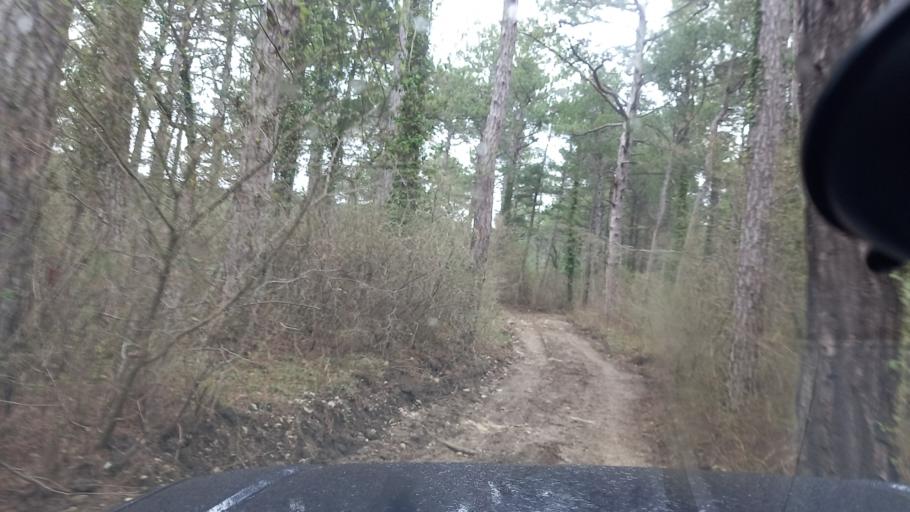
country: RU
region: Krasnodarskiy
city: Arkhipo-Osipovka
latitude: 44.3694
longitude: 38.4722
